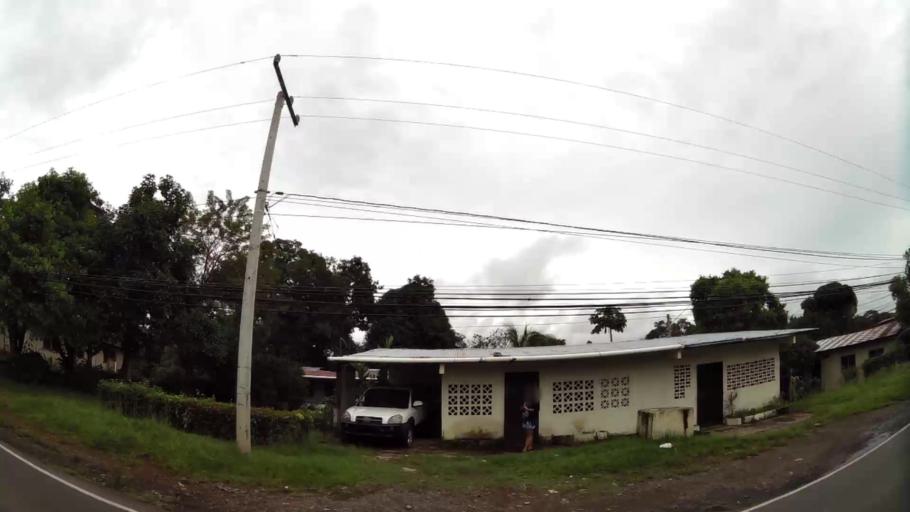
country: PA
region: Chiriqui
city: David
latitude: 8.4369
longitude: -82.4217
